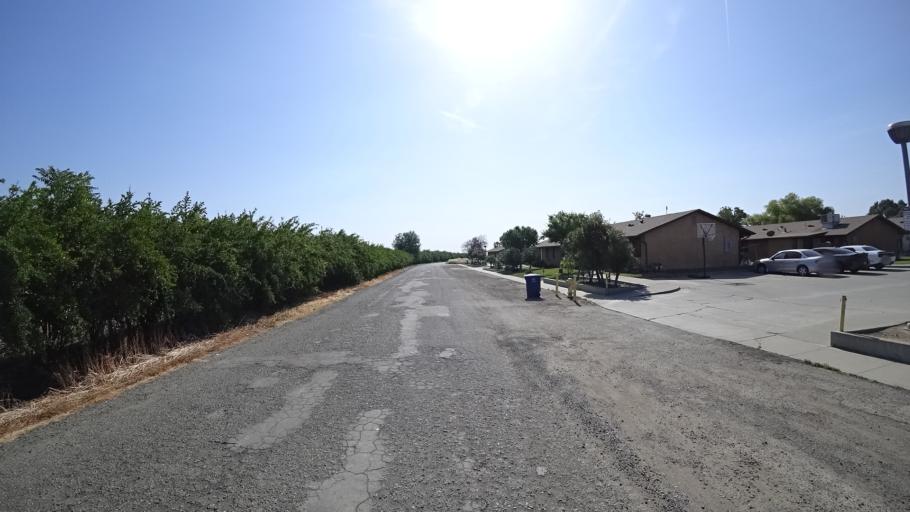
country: US
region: California
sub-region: Kings County
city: Kettleman City
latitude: 36.0118
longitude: -119.9623
